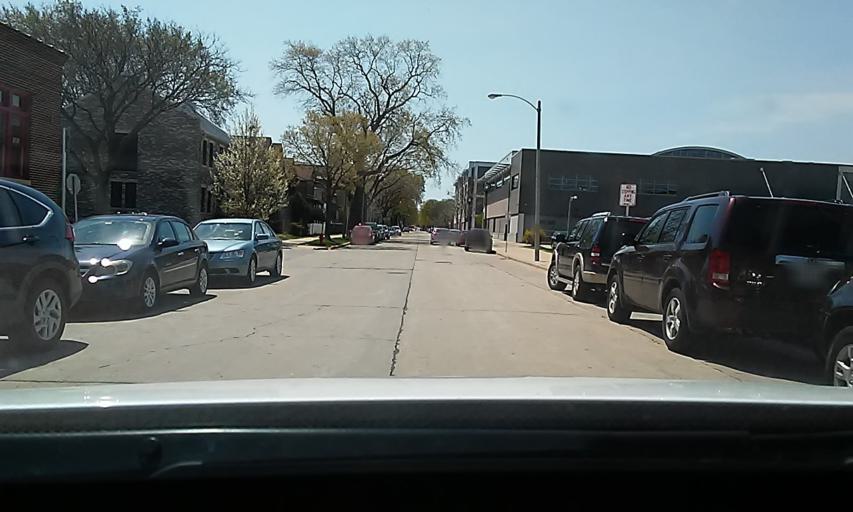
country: US
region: Wisconsin
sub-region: Milwaukee County
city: Milwaukee
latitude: 43.0256
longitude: -87.9140
